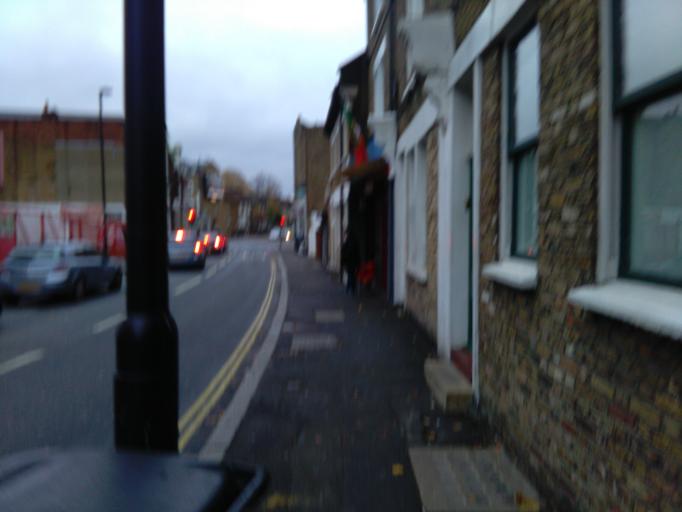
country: GB
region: England
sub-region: Greater London
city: Brixton
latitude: 51.4684
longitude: -0.1201
